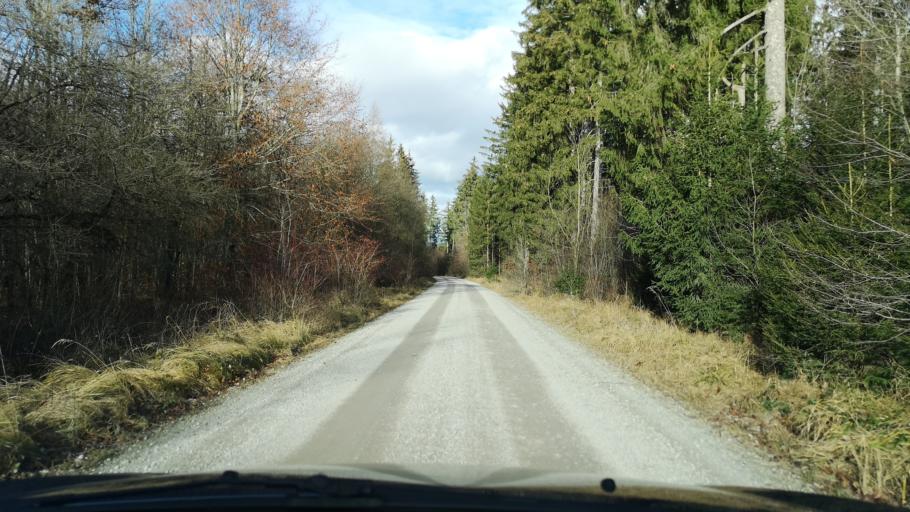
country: DE
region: Bavaria
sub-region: Upper Bavaria
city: Forstinning
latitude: 48.1184
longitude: 11.9088
